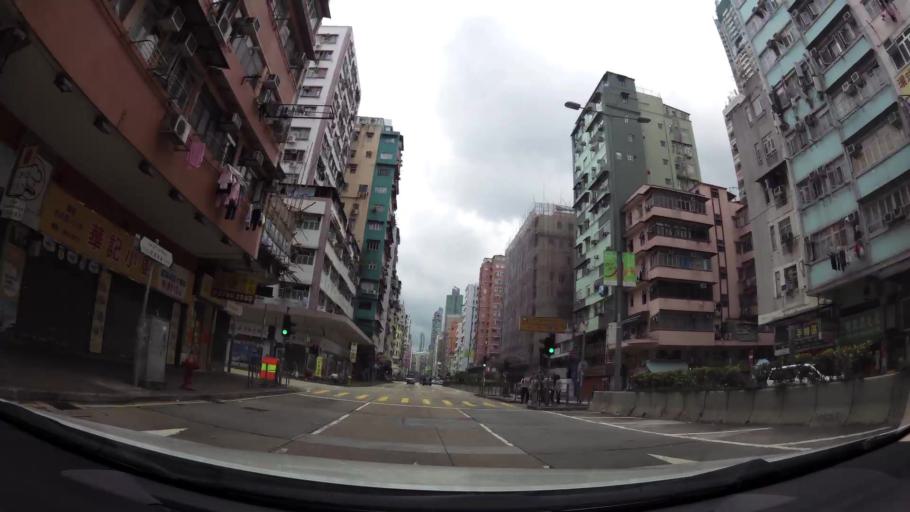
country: HK
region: Sham Shui Po
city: Sham Shui Po
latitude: 22.3272
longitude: 114.1625
